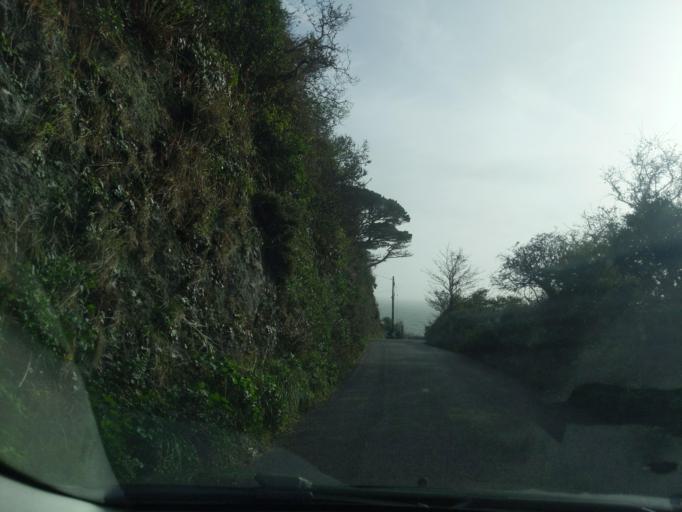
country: GB
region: England
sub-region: Cornwall
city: Looe
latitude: 50.3623
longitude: -4.3600
